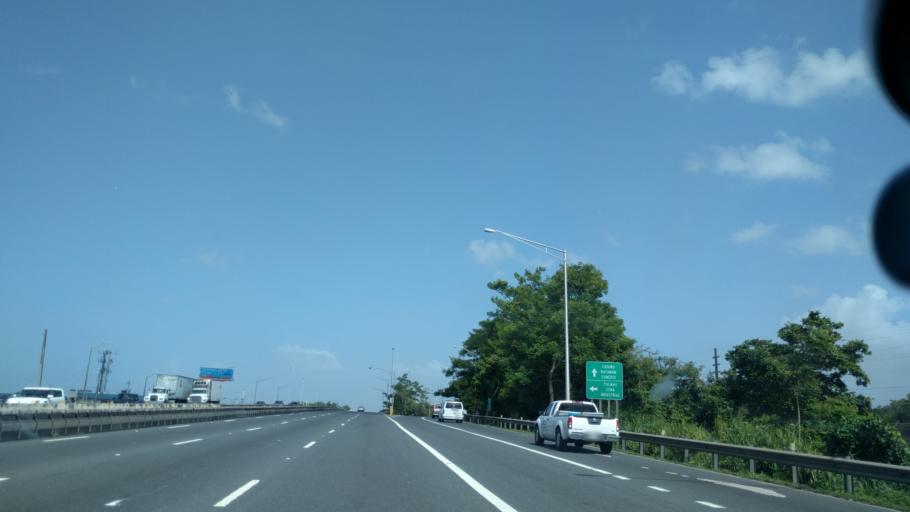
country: PR
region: Bayamon
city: Bayamon
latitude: 18.4225
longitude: -66.1494
